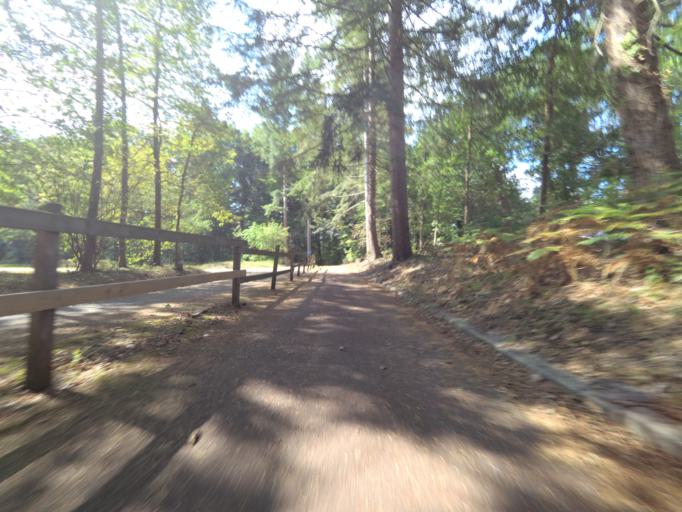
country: NL
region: Overijssel
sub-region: Gemeente Oldenzaal
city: Oldenzaal
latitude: 52.3073
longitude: 6.8839
